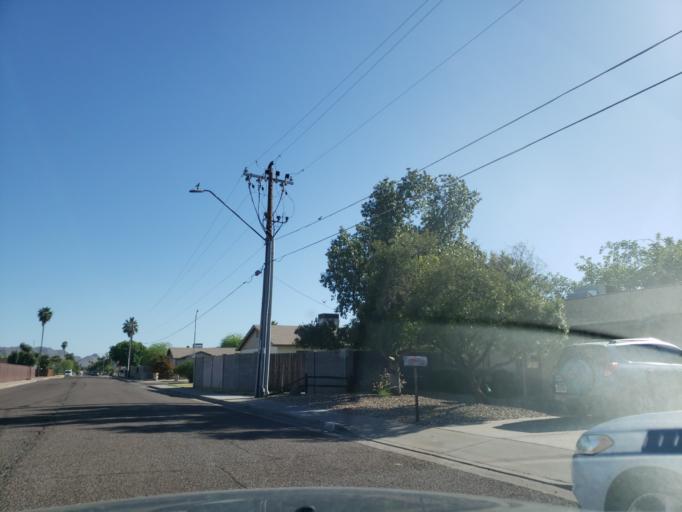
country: US
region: Arizona
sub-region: Maricopa County
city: Paradise Valley
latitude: 33.6240
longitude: -112.0004
